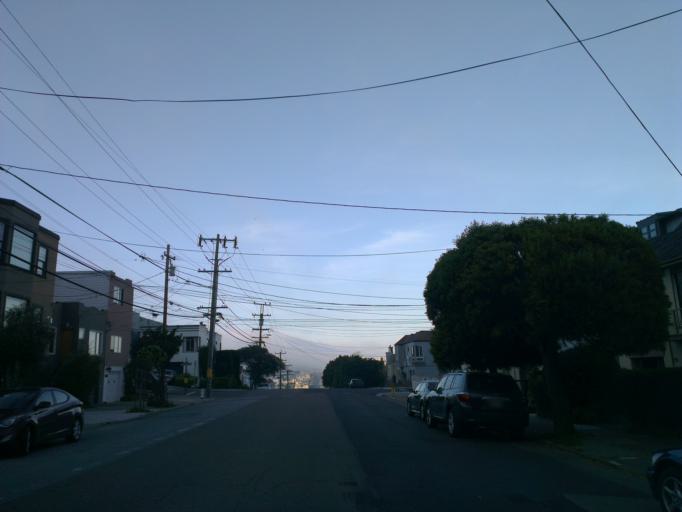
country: US
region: California
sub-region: San Francisco County
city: San Francisco
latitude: 37.7458
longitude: -122.4358
